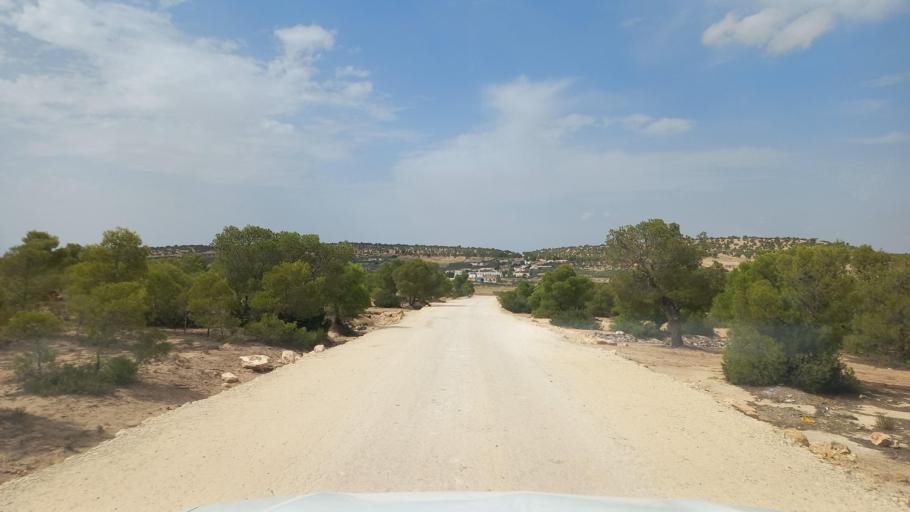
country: TN
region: Al Qasrayn
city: Kasserine
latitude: 35.3847
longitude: 8.8669
